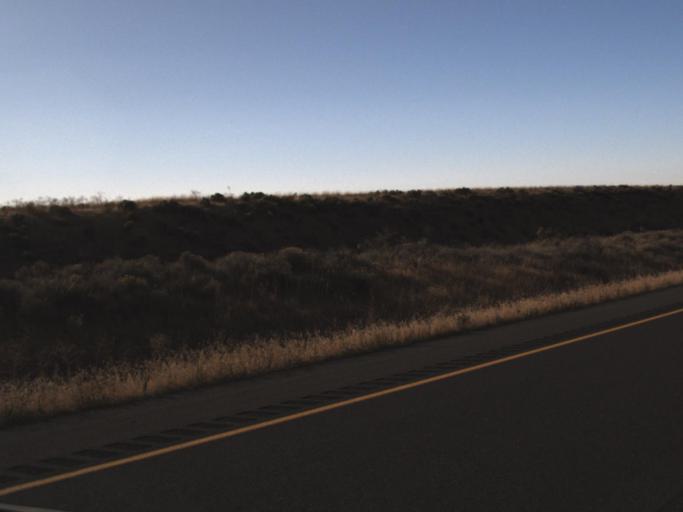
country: US
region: Washington
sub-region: Franklin County
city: Connell
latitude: 46.6921
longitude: -118.8382
